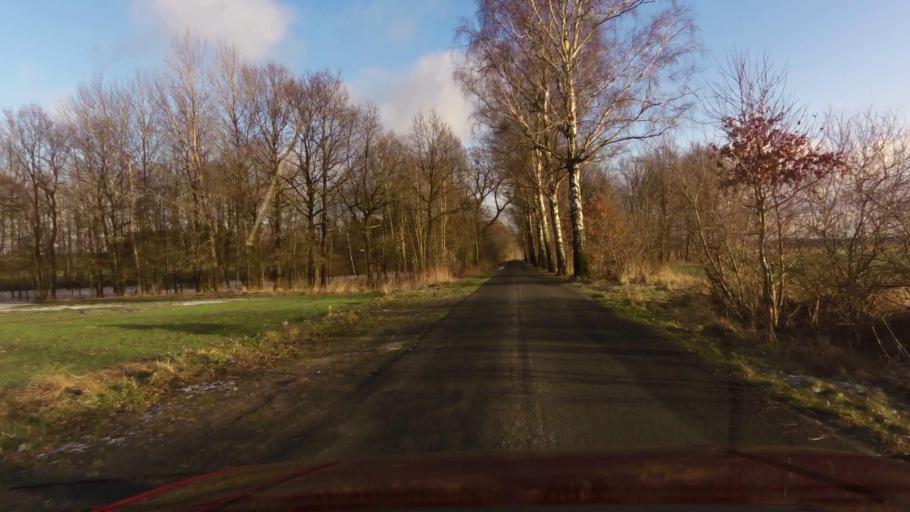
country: PL
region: West Pomeranian Voivodeship
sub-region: Koszalin
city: Koszalin
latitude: 54.0713
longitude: 16.1471
